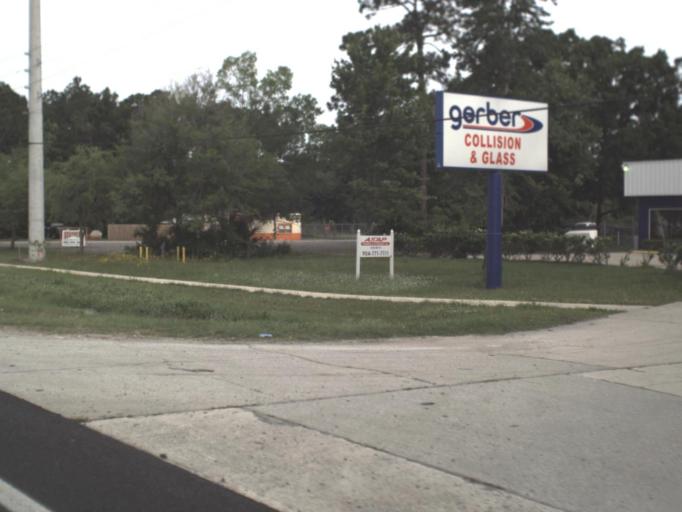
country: US
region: Florida
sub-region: Saint Johns County
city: Saint Augustine
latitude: 29.9150
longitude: -81.3999
